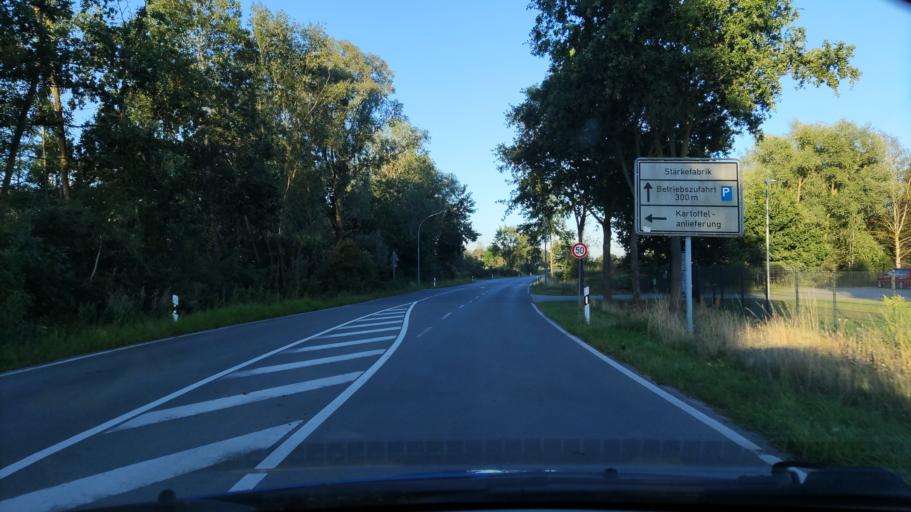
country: DE
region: Lower Saxony
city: Luechow
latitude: 52.9819
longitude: 11.1570
